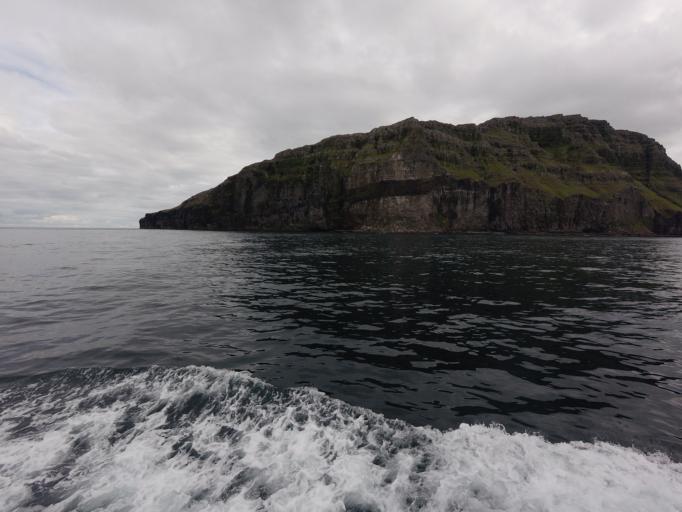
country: FO
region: Nordoyar
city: Klaksvik
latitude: 62.3082
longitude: -6.3487
